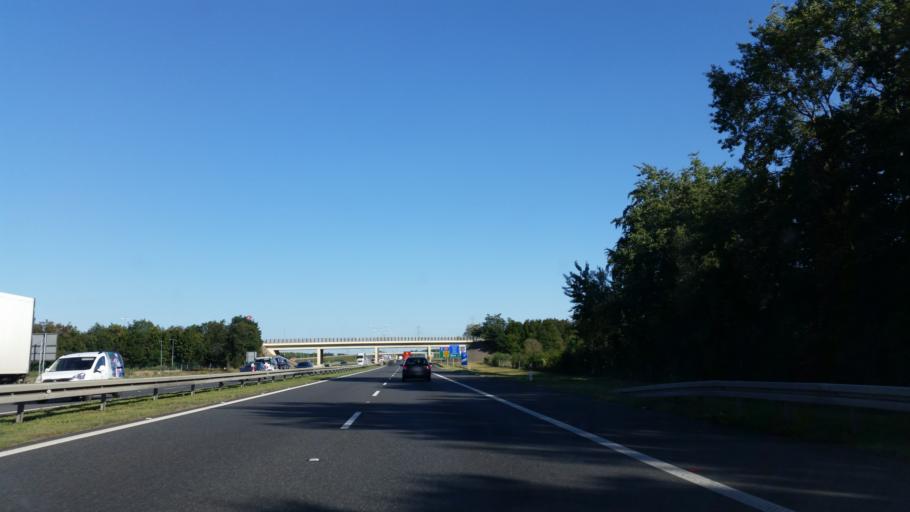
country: PL
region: Opole Voivodeship
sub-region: Powiat brzeski
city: Grodkow
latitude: 50.7855
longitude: 17.3424
